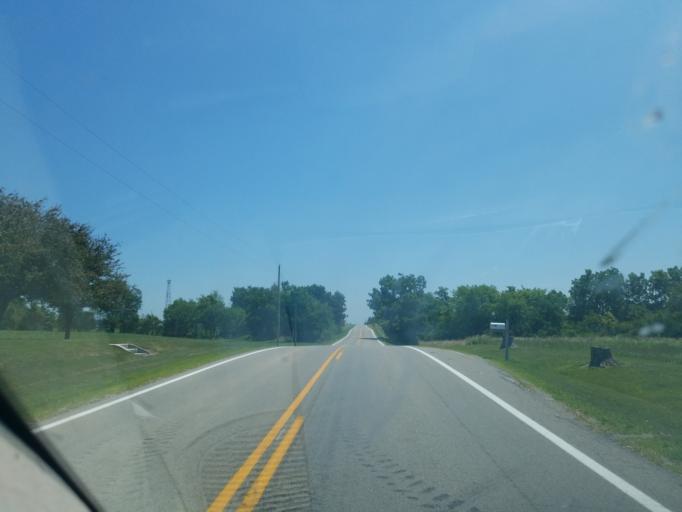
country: US
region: Ohio
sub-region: Mercer County
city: Rockford
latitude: 40.7424
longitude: -84.7113
